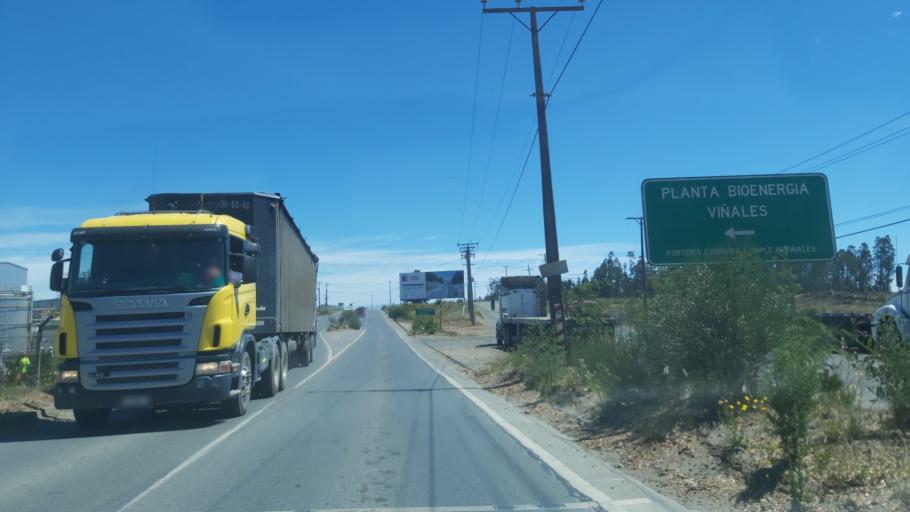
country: CL
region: Maule
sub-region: Provincia de Talca
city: Constitucion
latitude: -35.3692
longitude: -72.4108
